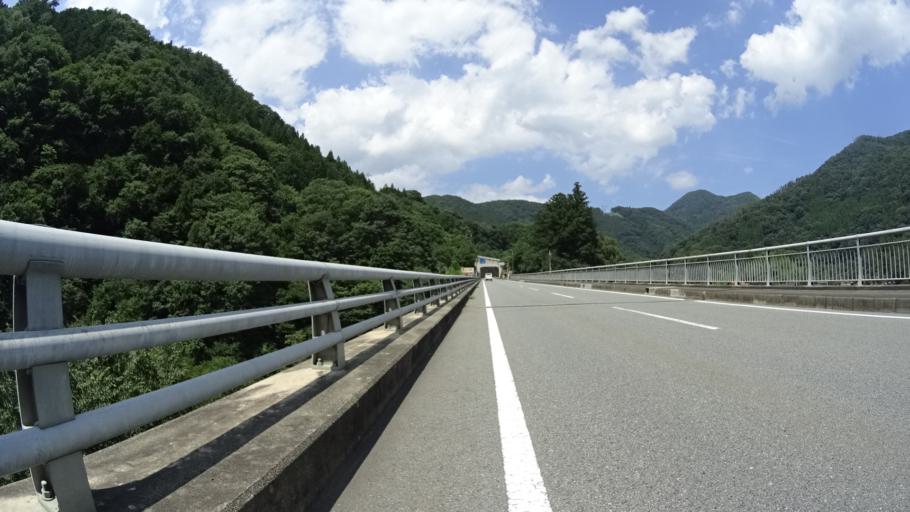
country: JP
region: Gunma
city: Tomioka
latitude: 36.0800
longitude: 138.7769
